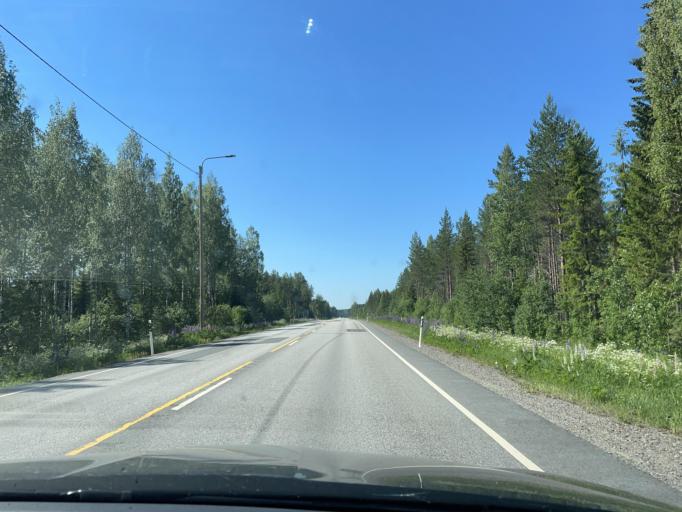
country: FI
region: Central Finland
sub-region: Saarijaervi-Viitasaari
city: Viitasaari
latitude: 63.1776
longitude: 26.0303
